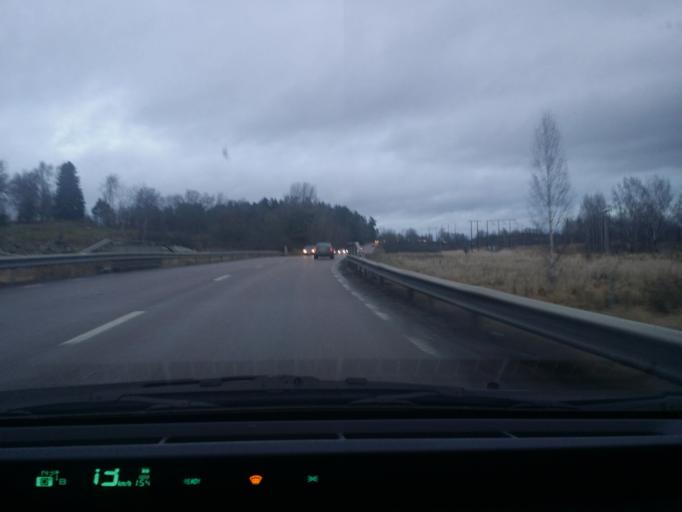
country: SE
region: Soedermanland
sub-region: Eskilstuna Kommun
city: Torshalla
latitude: 59.3792
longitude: 16.4606
